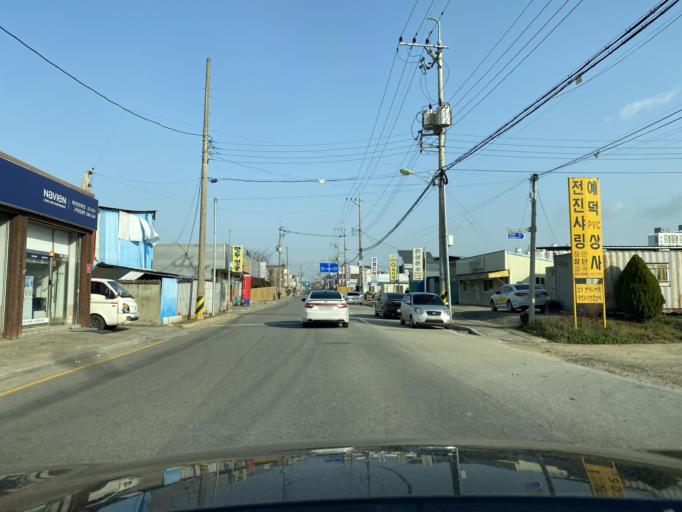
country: KR
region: Chungcheongnam-do
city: Yesan
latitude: 36.6800
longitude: 126.8289
